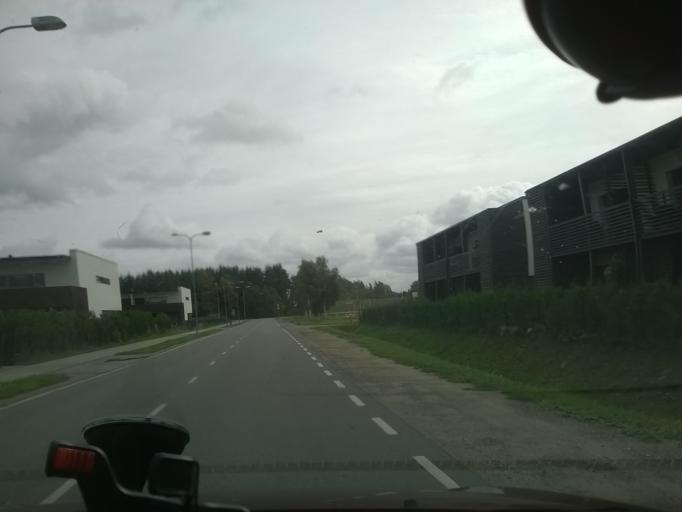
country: EE
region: Harju
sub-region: Tallinna linn
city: Tallinn
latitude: 59.4006
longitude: 24.8097
